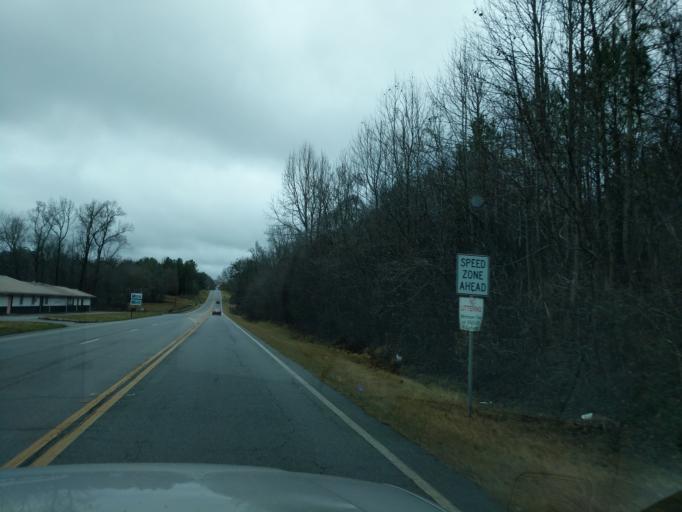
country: US
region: Georgia
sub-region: Hart County
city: Royston
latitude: 34.3302
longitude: -83.1097
